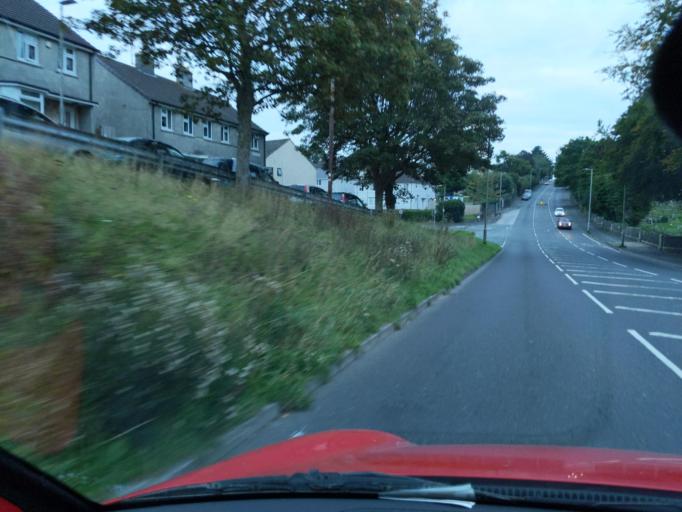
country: GB
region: England
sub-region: Cornwall
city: Millbrook
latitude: 50.3992
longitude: -4.1703
